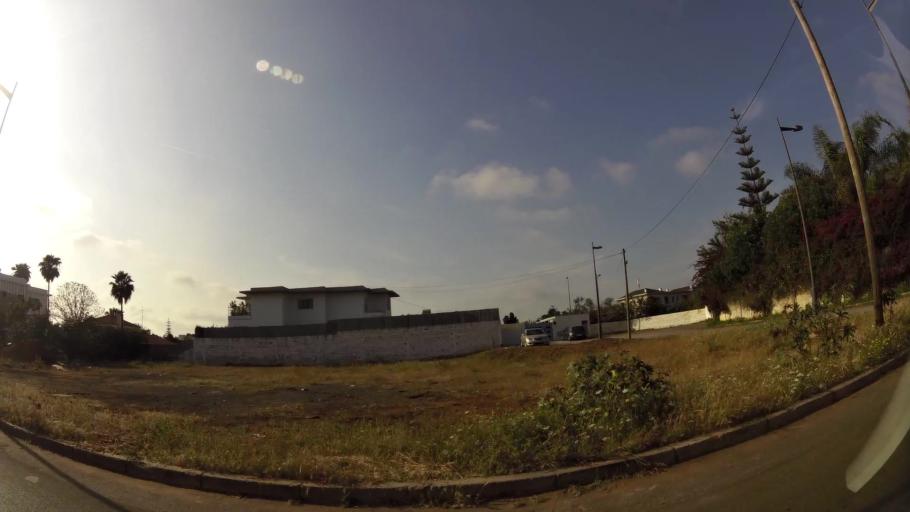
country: MA
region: Rabat-Sale-Zemmour-Zaer
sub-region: Rabat
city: Rabat
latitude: 33.9415
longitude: -6.8169
